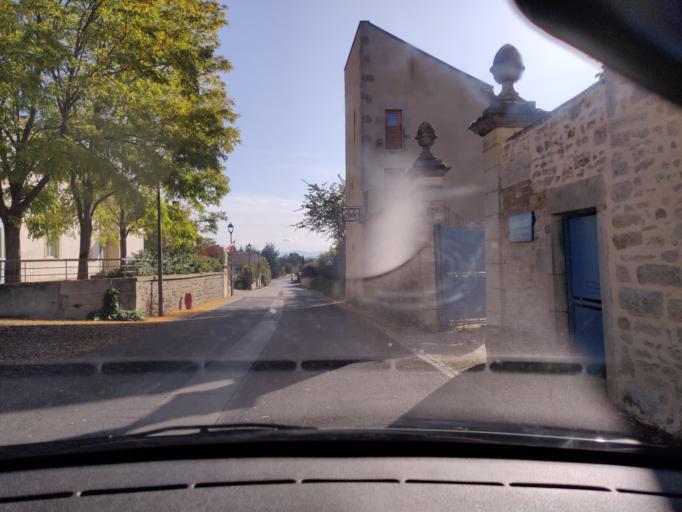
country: FR
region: Auvergne
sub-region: Departement du Puy-de-Dome
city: Aigueperse
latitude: 46.0316
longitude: 3.1787
